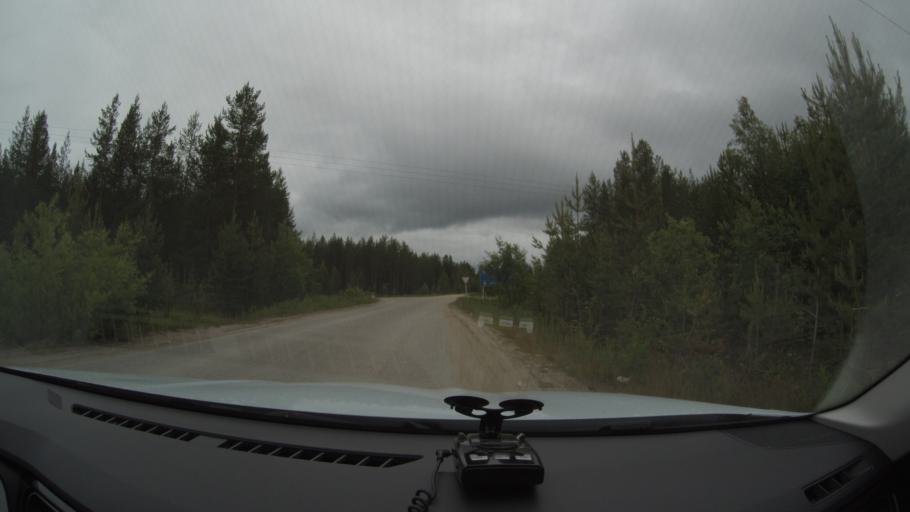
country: RU
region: Komi Republic
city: Kozhva
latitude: 65.1159
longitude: 57.0006
